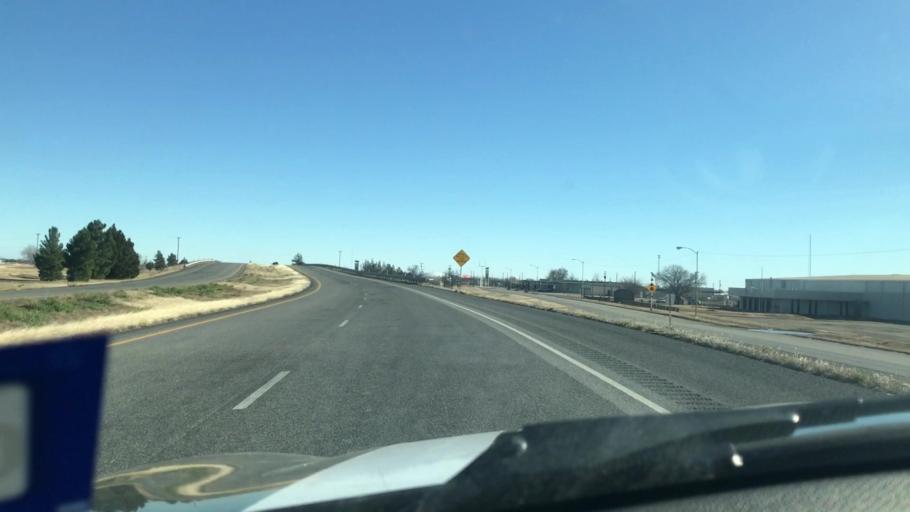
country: US
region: Texas
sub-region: Scurry County
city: Snyder
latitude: 32.7413
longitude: -100.9212
